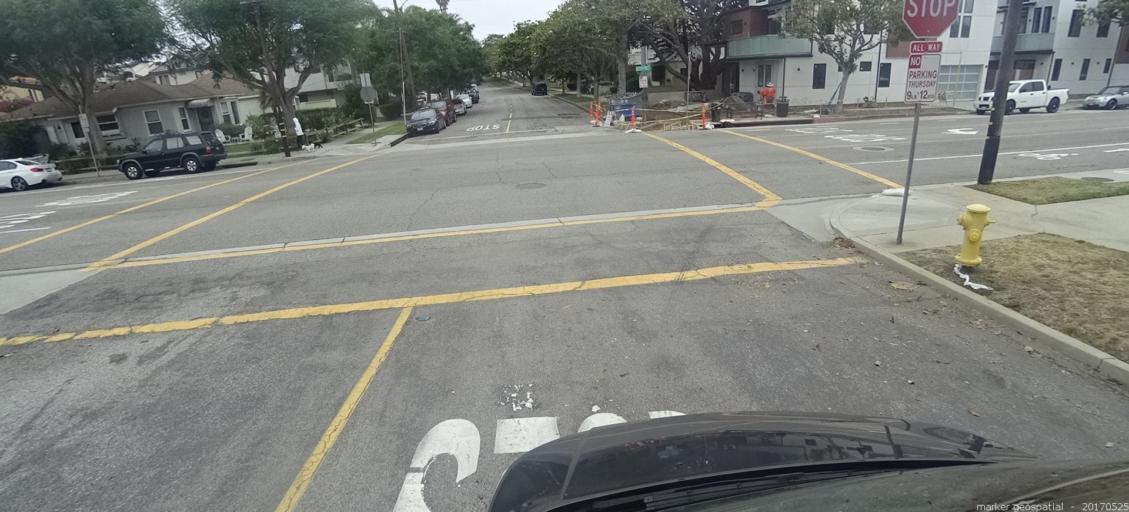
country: US
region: California
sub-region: Los Angeles County
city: Redondo Beach
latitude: 33.8493
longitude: -118.3814
